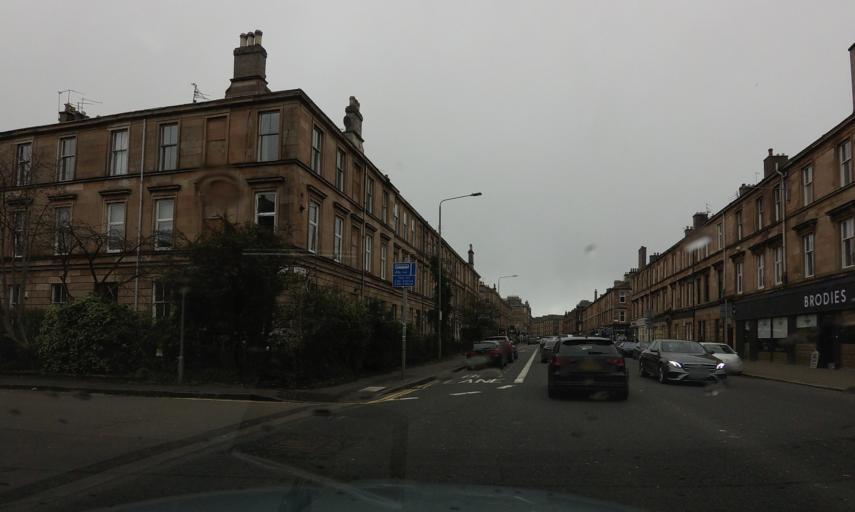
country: GB
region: Scotland
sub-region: Glasgow City
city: Glasgow
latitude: 55.8351
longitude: -4.2726
